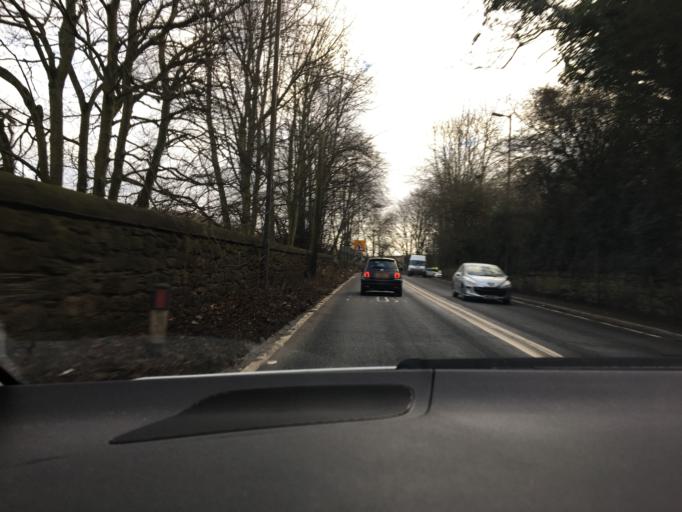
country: GB
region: Scotland
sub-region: Midlothian
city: Dalkeith
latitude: 55.8747
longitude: -3.0804
